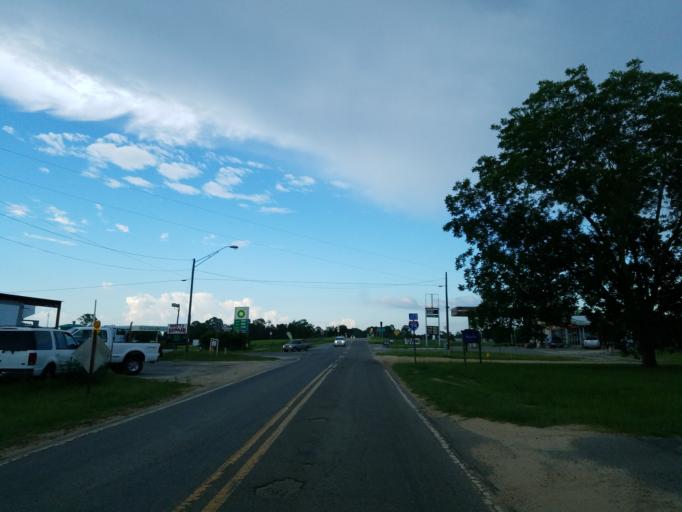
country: US
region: Georgia
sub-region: Cook County
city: Sparks
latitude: 31.2674
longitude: -83.4739
